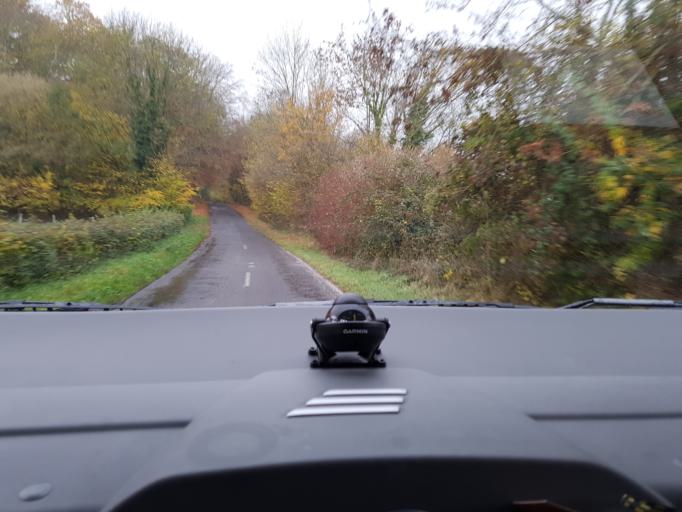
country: FR
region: Haute-Normandie
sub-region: Departement de la Seine-Maritime
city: Petiville
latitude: 49.4279
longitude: 0.6207
